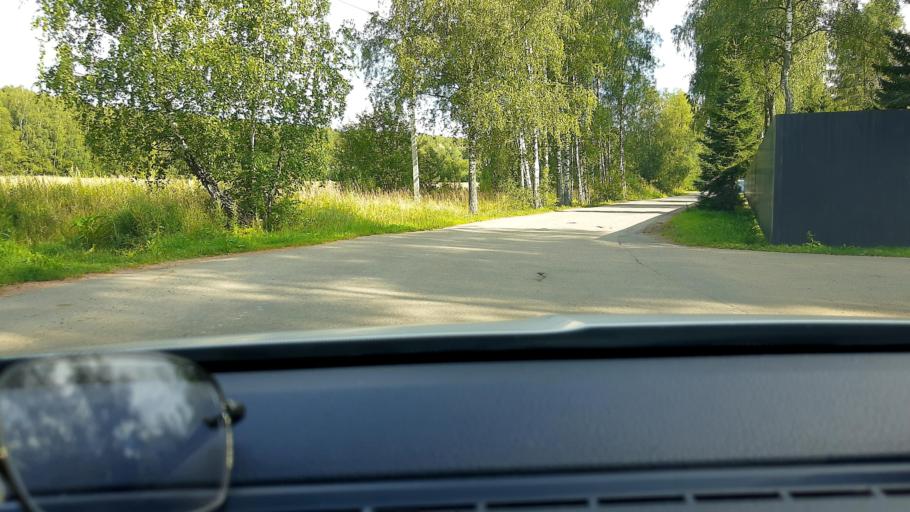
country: RU
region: Moskovskaya
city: Nekrasovskiy
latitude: 56.0976
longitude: 37.5351
